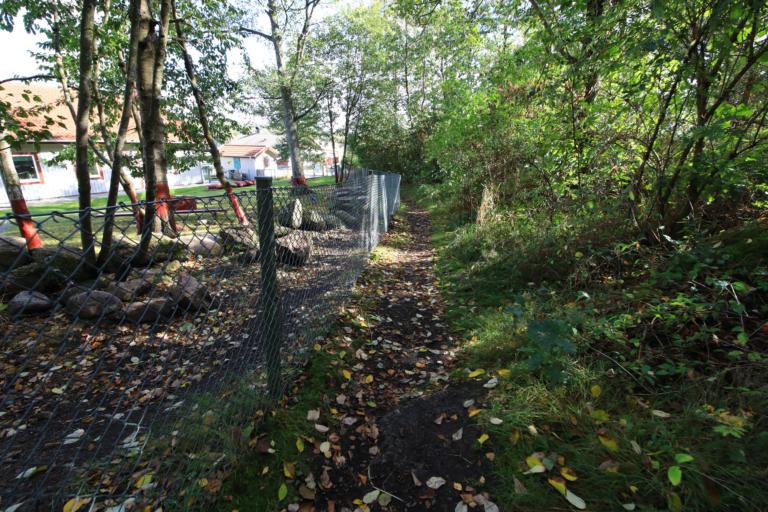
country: SE
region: Halland
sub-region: Varbergs Kommun
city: Varberg
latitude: 57.1761
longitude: 12.2218
